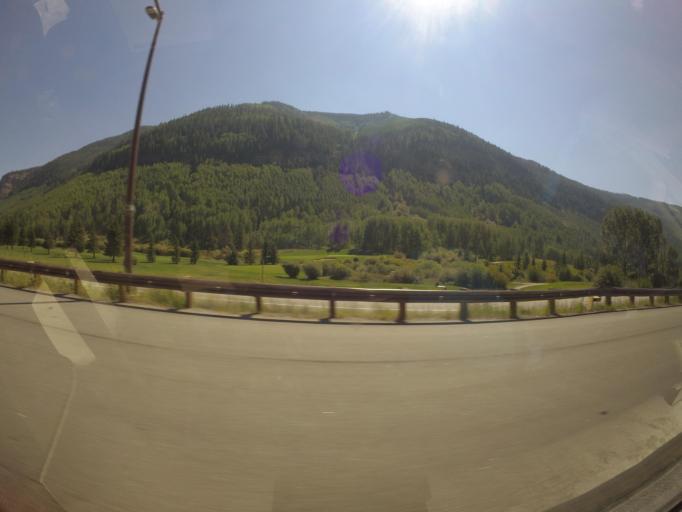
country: US
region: Colorado
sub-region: Eagle County
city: Vail
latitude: 39.6469
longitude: -106.3319
